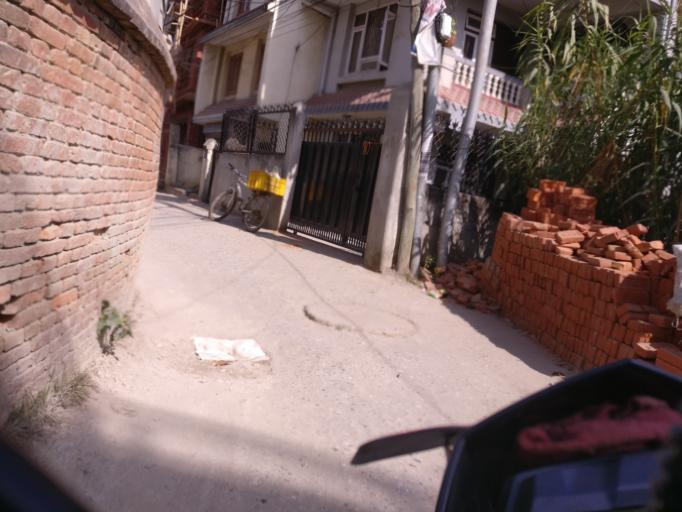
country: NP
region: Central Region
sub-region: Bagmati Zone
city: Patan
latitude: 27.6656
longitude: 85.3291
